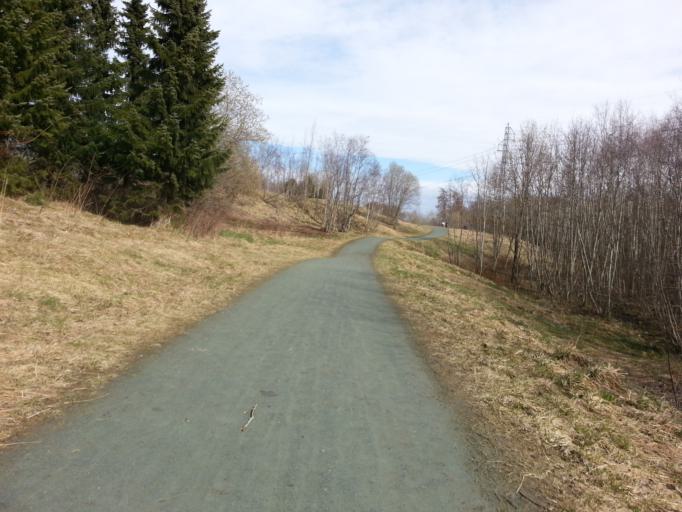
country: NO
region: Sor-Trondelag
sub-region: Trondheim
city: Trondheim
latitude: 63.4165
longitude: 10.4387
